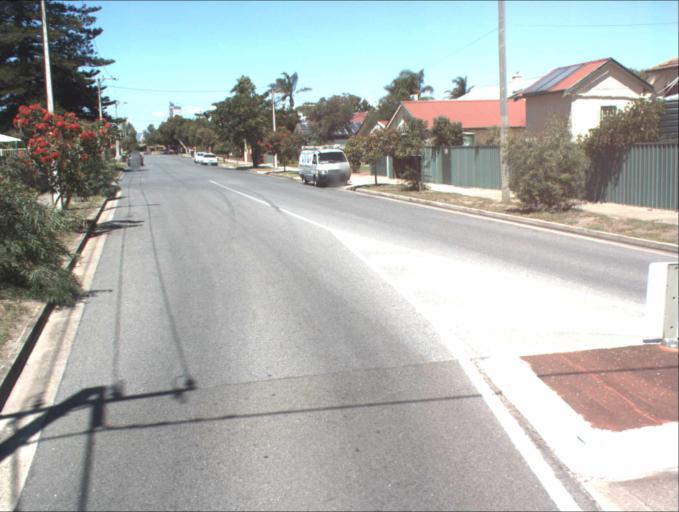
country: AU
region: South Australia
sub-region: Port Adelaide Enfield
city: Birkenhead
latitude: -34.8245
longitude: 138.4871
